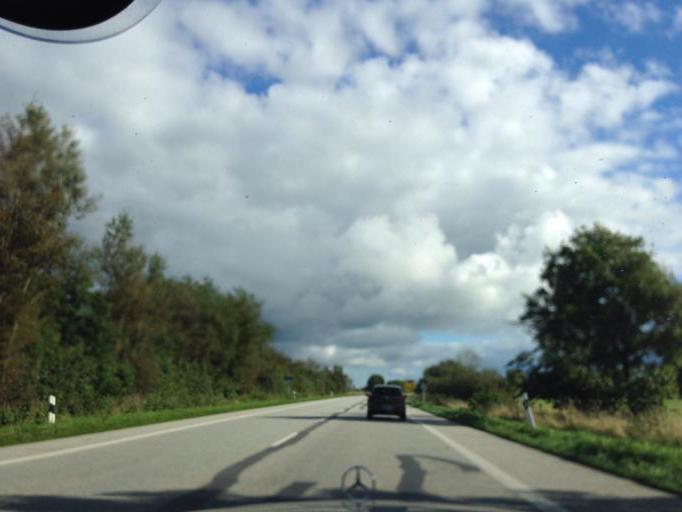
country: DE
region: Schleswig-Holstein
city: Stedesand
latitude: 54.7506
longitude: 8.9058
